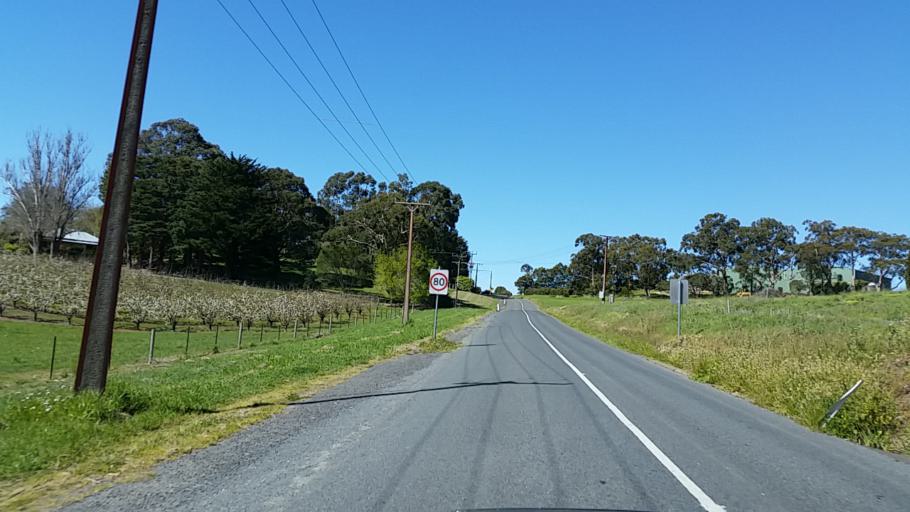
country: AU
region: South Australia
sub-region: Adelaide Hills
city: Bridgewater
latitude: -34.9561
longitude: 138.7522
